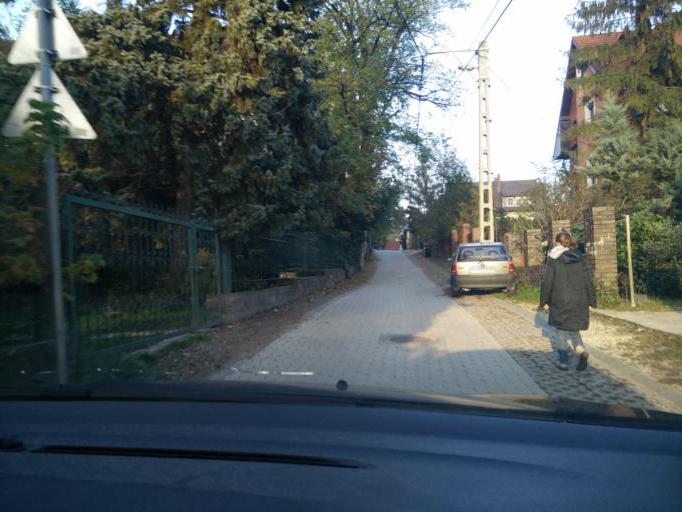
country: HU
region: Pest
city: Piliscsaba
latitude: 47.6333
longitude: 18.8412
